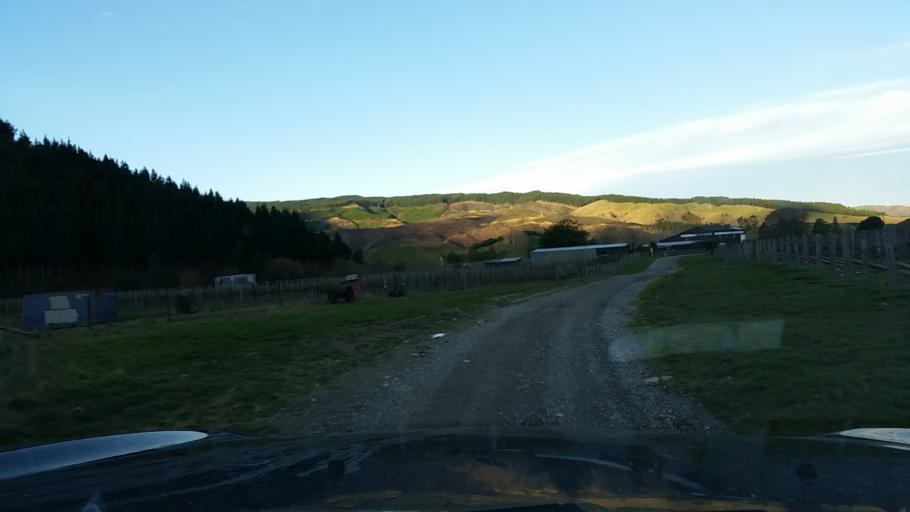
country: NZ
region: Nelson
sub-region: Nelson City
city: Nelson
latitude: -41.5043
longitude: 173.5748
